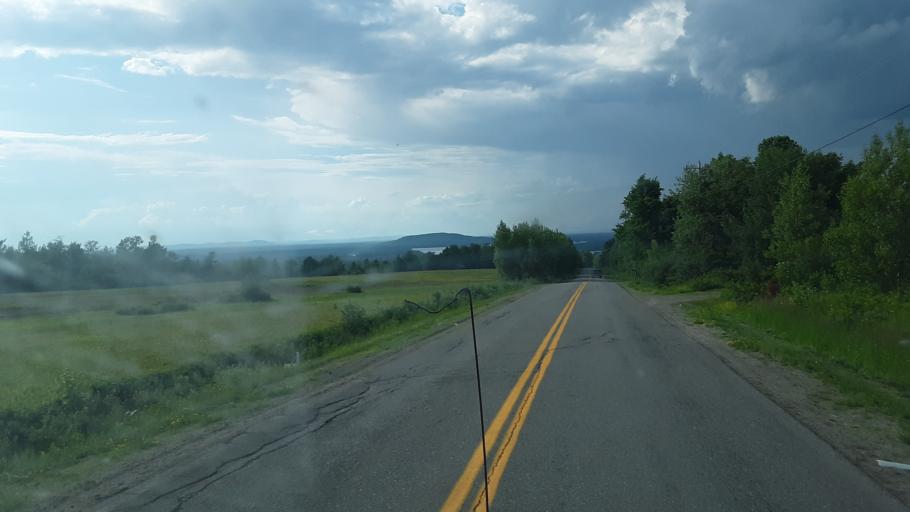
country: US
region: Maine
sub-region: Washington County
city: Calais
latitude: 45.0951
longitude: -67.5077
